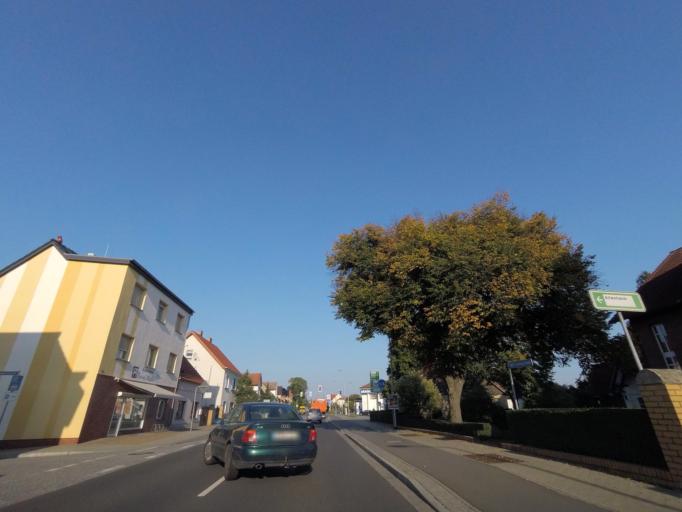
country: DE
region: Saxony-Anhalt
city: Jessen
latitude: 51.7923
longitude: 12.9611
